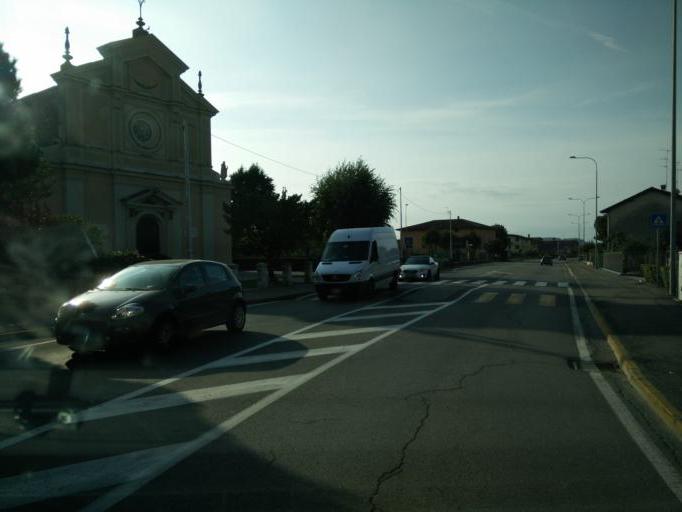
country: IT
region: Lombardy
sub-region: Provincia di Brescia
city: Colombaro-Timoline
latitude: 45.6366
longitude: 10.0100
